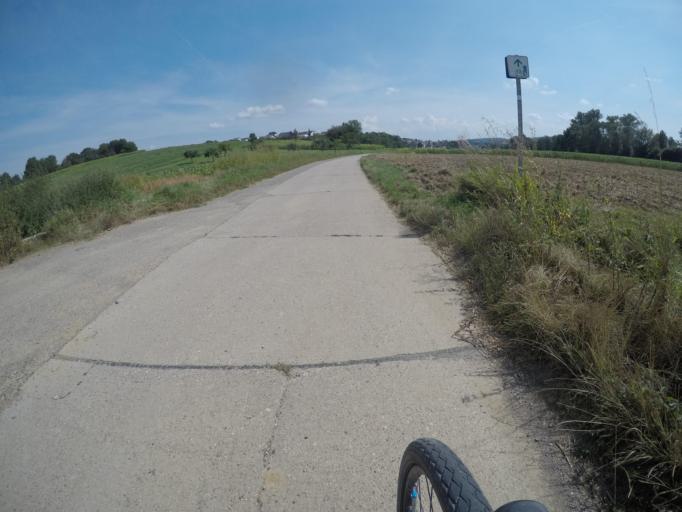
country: DE
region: Baden-Wuerttemberg
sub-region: Karlsruhe Region
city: Gondelsheim
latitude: 49.0492
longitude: 8.6719
